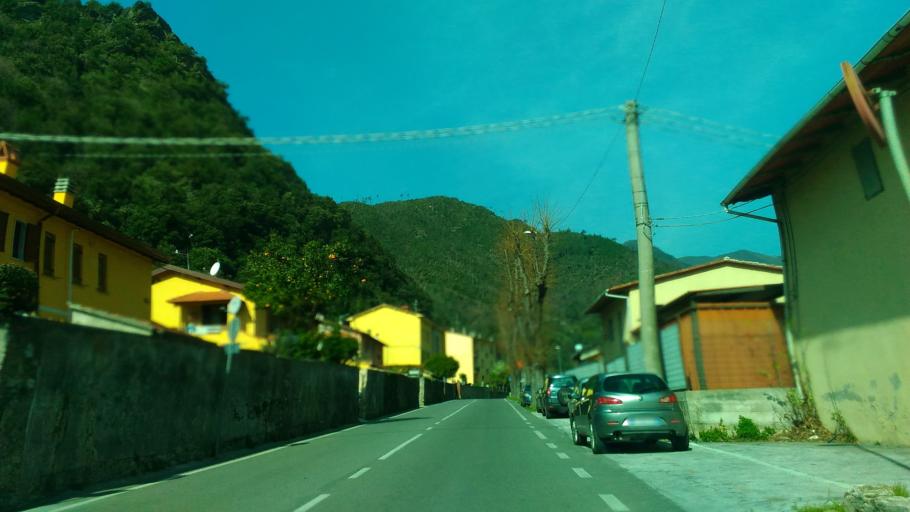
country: IT
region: Tuscany
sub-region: Provincia di Lucca
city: Seravezza
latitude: 43.9872
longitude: 10.2267
